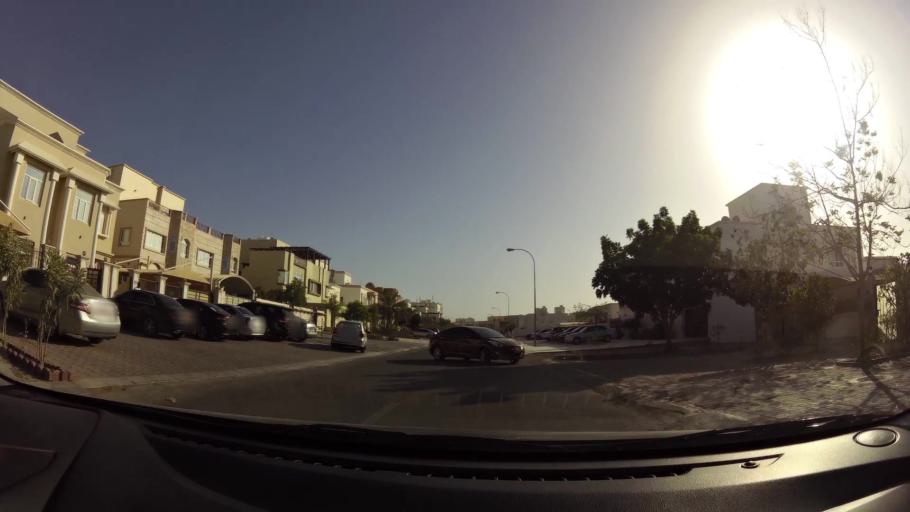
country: OM
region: Muhafazat Masqat
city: As Sib al Jadidah
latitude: 23.6012
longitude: 58.2080
